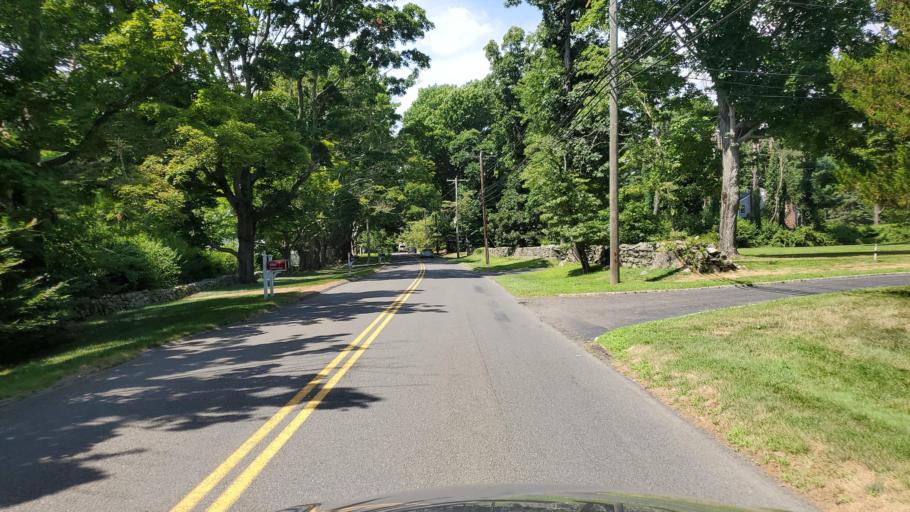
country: US
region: Connecticut
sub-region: Fairfield County
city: Southport
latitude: 41.1916
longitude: -73.3085
